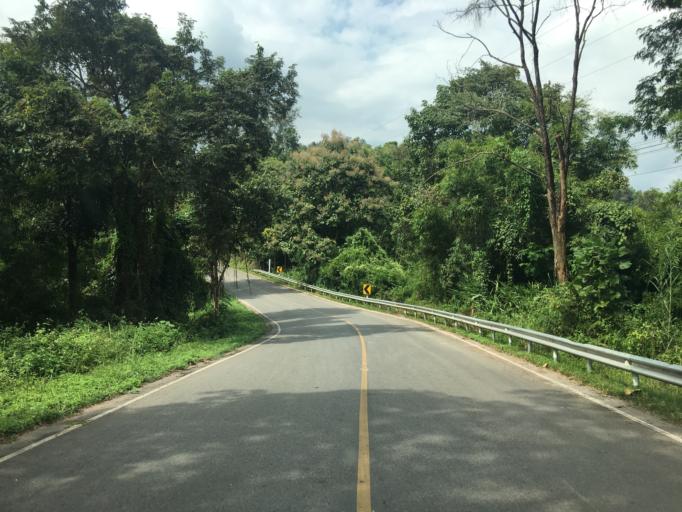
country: TH
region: Nan
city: Ban Luang
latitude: 18.8722
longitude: 100.5466
